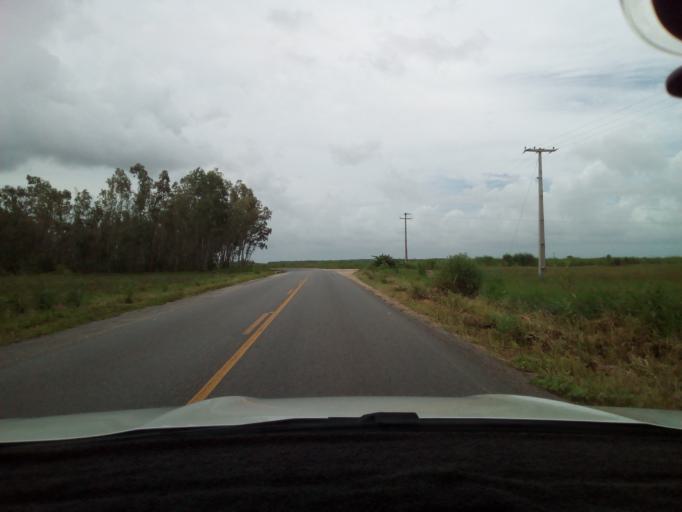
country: BR
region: Paraiba
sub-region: Pedras De Fogo
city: Pedras de Fogo
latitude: -7.3759
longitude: -35.0360
